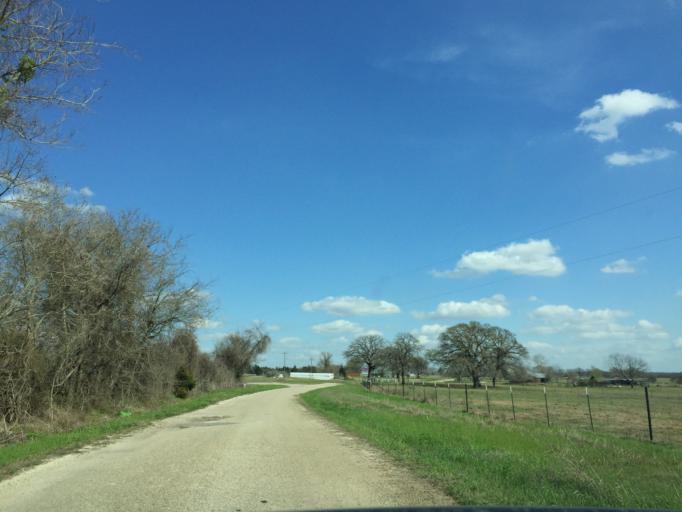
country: US
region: Texas
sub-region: Milam County
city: Thorndale
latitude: 30.5938
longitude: -97.1345
